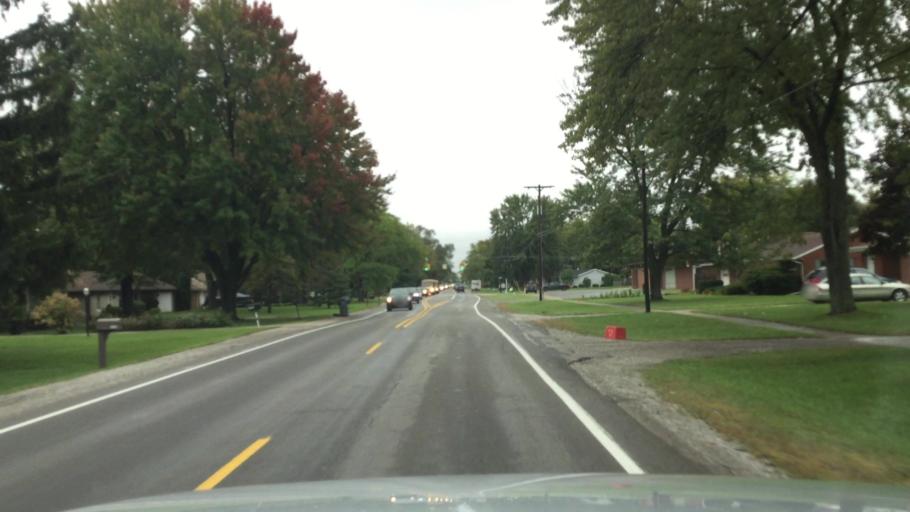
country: US
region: Michigan
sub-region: Saginaw County
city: Shields
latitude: 43.4456
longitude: -84.0050
